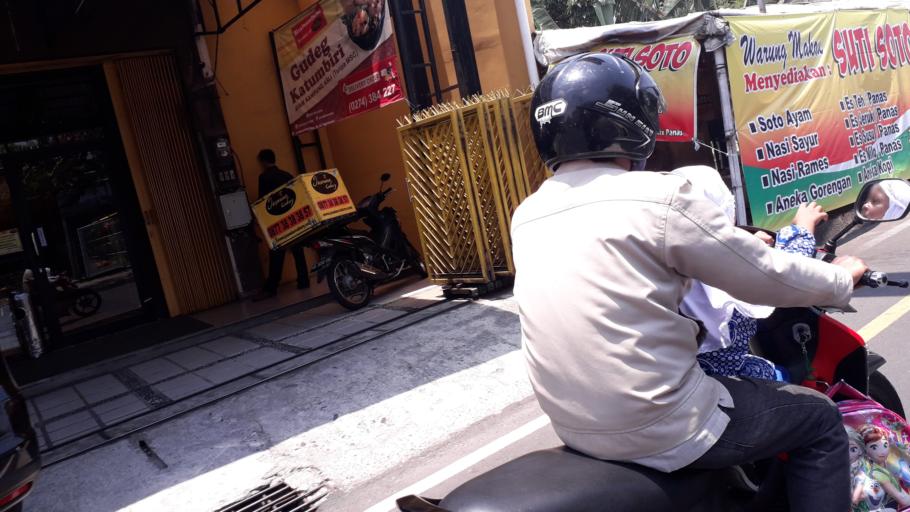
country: ID
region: Daerah Istimewa Yogyakarta
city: Yogyakarta
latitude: -7.7698
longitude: 110.3686
